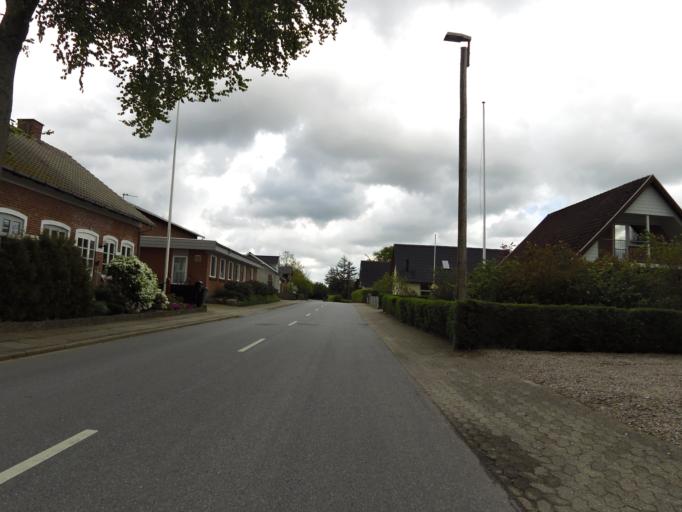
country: DK
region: South Denmark
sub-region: Haderslev Kommune
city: Gram
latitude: 55.3169
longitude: 8.9792
